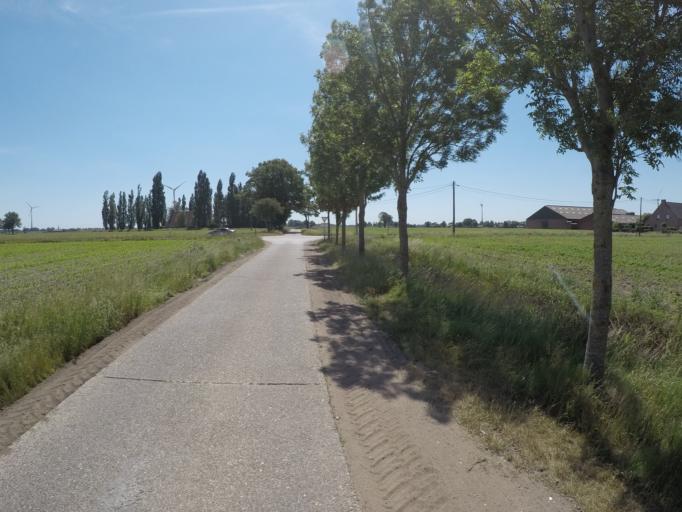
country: NL
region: North Brabant
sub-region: Gemeente Zundert
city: Zundert
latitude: 51.4089
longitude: 4.6750
